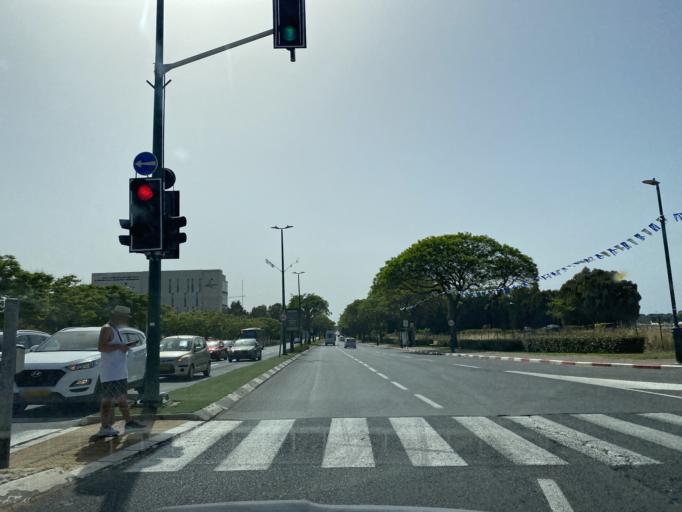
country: IL
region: Tel Aviv
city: Herzliyya
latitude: 32.1774
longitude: 34.8398
